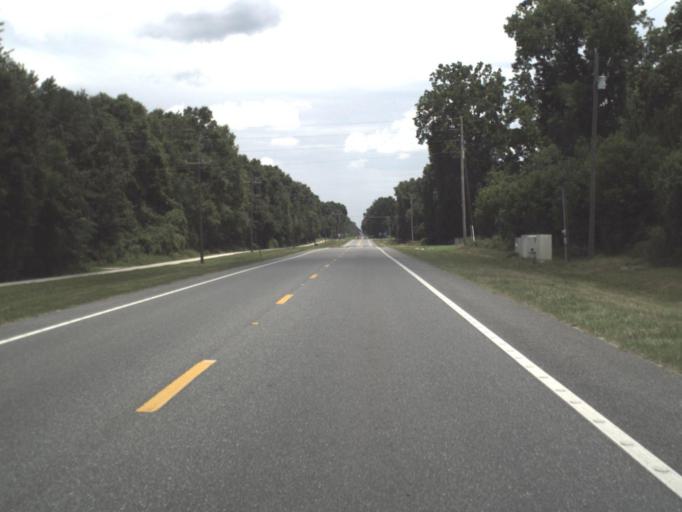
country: US
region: Florida
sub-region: Lafayette County
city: Mayo
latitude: 29.9947
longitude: -82.9355
